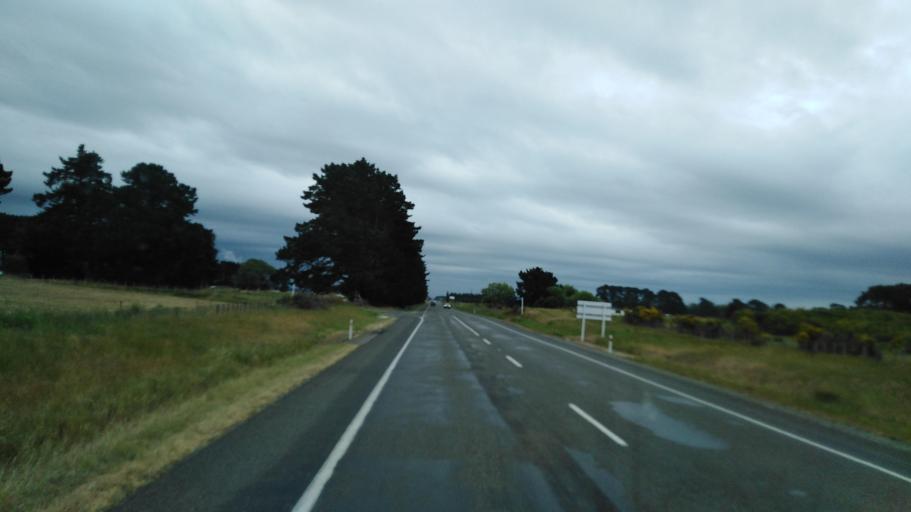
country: NZ
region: Manawatu-Wanganui
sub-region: Horowhenua District
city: Foxton
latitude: -40.4284
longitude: 175.3025
